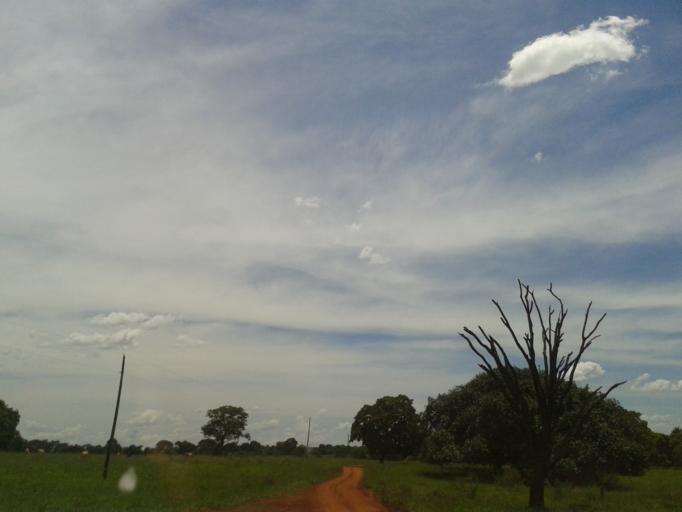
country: BR
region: Minas Gerais
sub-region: Capinopolis
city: Capinopolis
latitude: -18.8014
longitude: -49.7759
